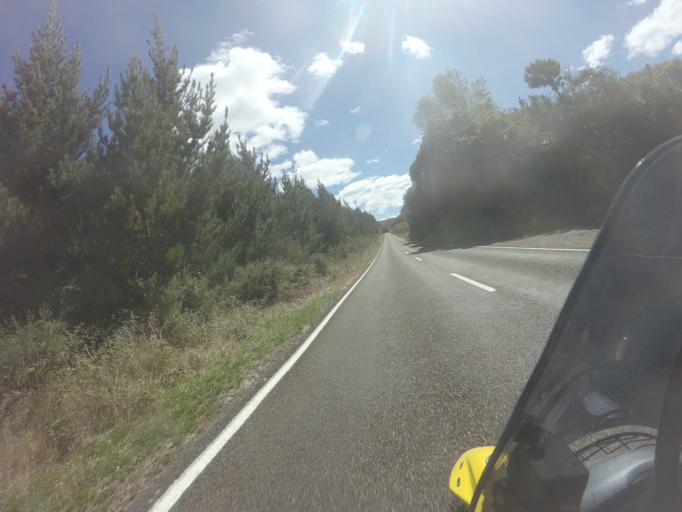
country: NZ
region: Bay of Plenty
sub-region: Kawerau District
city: Kawerau
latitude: -38.1680
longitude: 176.8140
